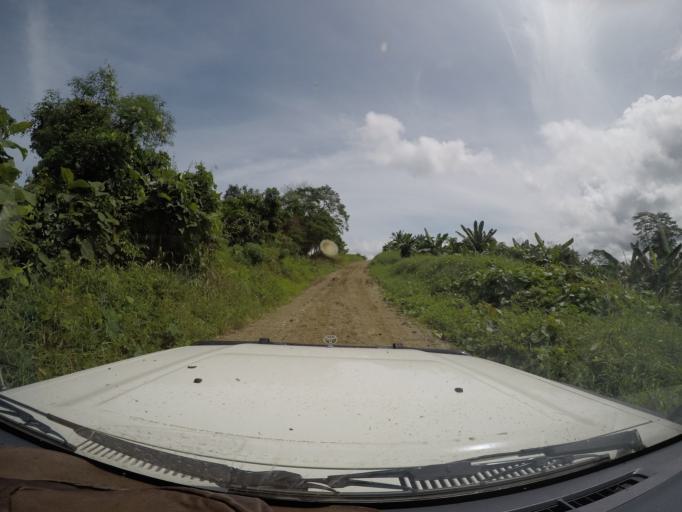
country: PG
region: Gulf
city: Kerema
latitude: -7.9884
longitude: 145.8287
